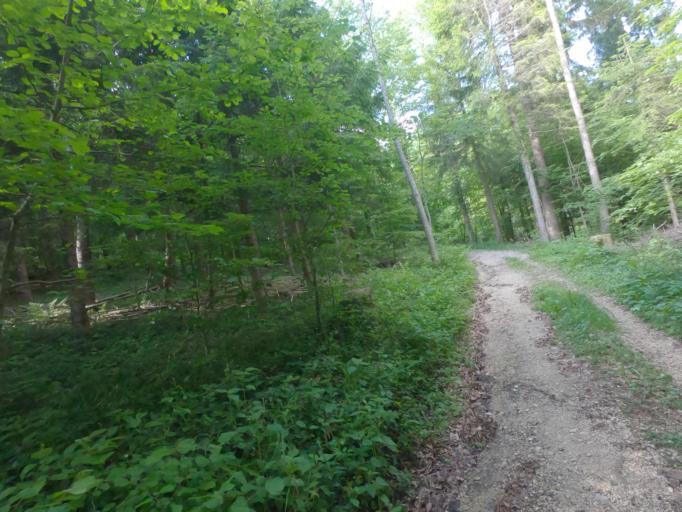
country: CH
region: Solothurn
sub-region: Bezirk Lebern
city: Riedholz
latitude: 47.2422
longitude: 7.5397
